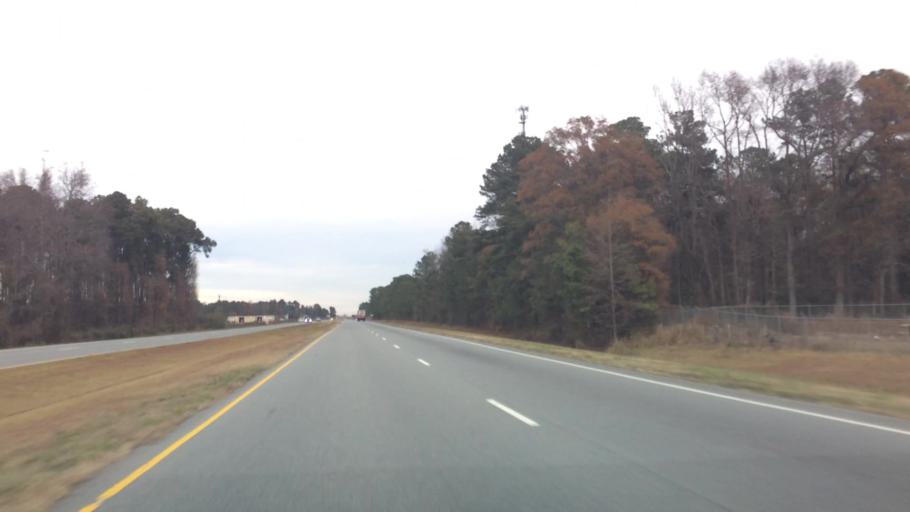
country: US
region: North Carolina
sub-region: Wayne County
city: Mount Olive
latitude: 35.1644
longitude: -78.1061
